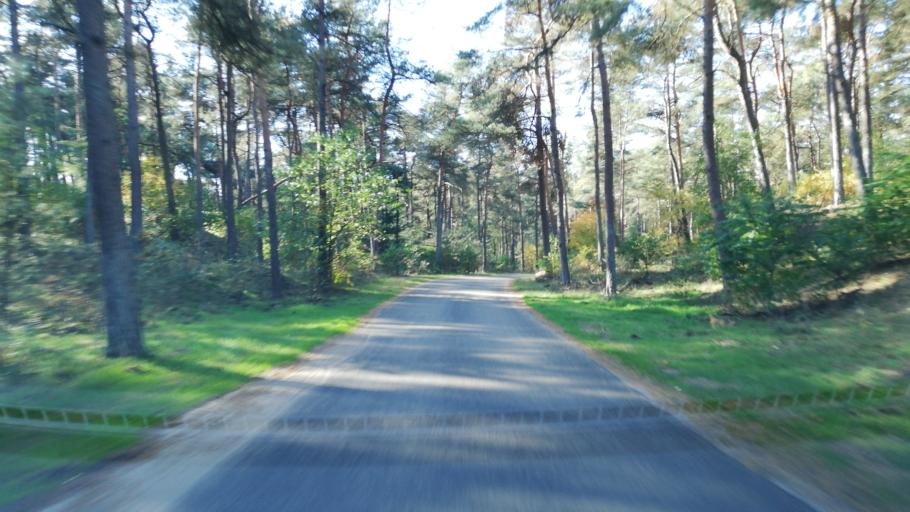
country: NL
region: Gelderland
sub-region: Gemeente Ede
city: Harskamp
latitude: 52.1723
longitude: 5.7535
